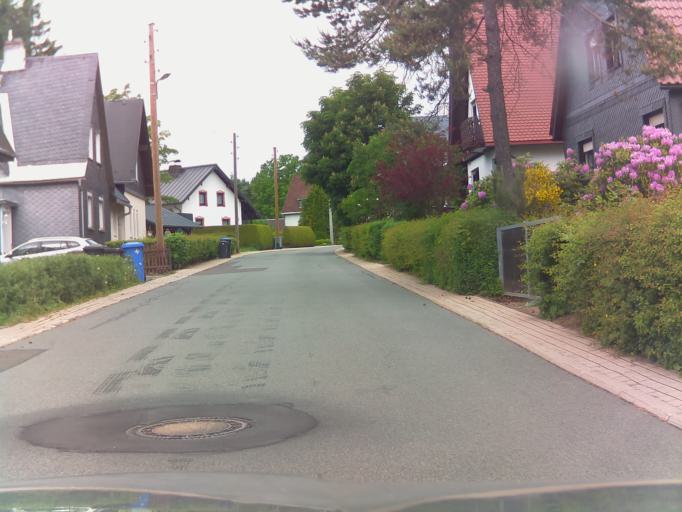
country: DE
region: Thuringia
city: Schmiedefeld am Rennsteig
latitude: 50.6062
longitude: 10.8099
